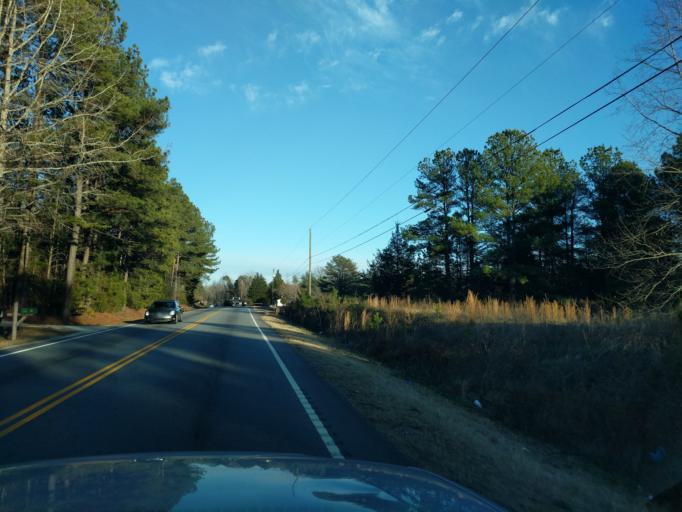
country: US
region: South Carolina
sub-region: Greenville County
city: Simpsonville
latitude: 34.6549
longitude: -82.2920
